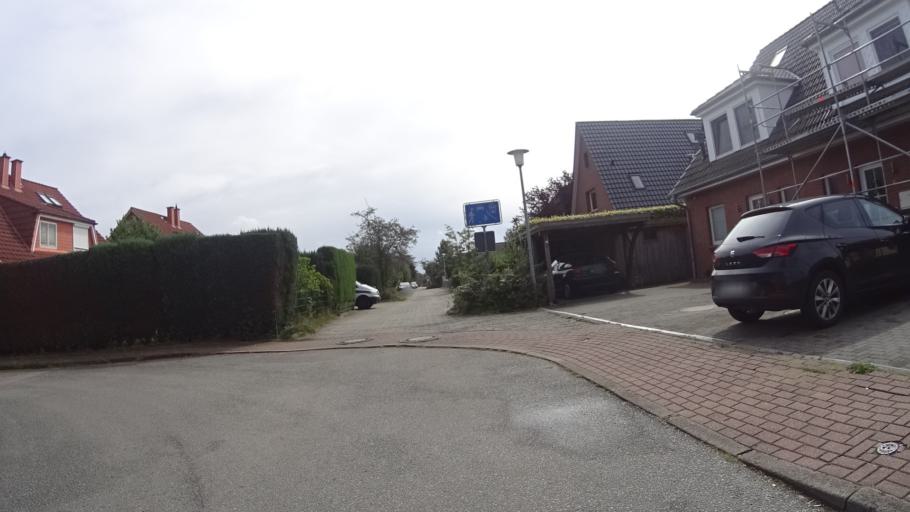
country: DE
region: Schleswig-Holstein
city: Henstedt-Ulzburg
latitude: 53.7589
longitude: 9.9983
